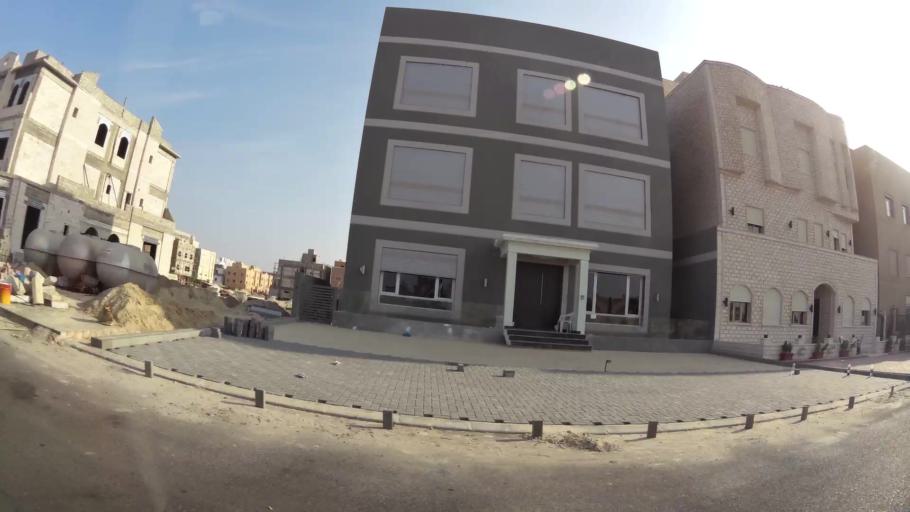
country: KW
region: Mubarak al Kabir
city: Mubarak al Kabir
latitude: 29.1857
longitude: 48.1051
